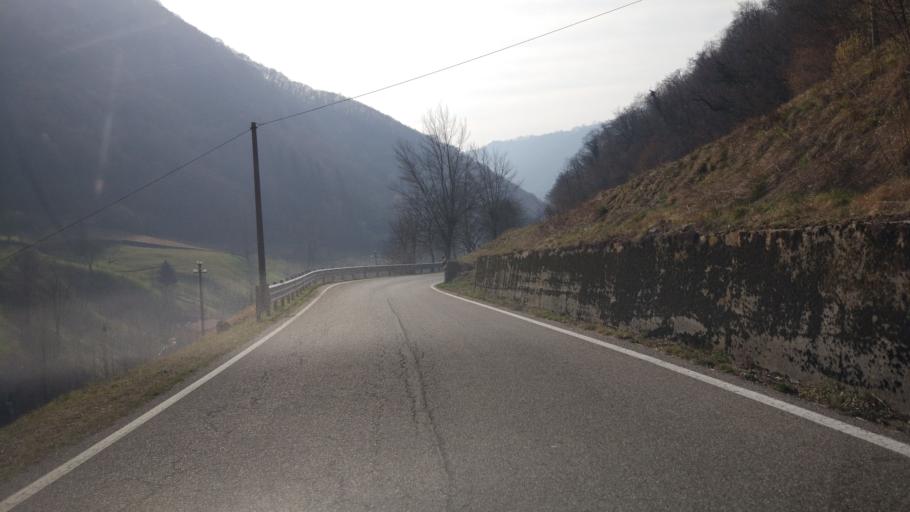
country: IT
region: Veneto
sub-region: Provincia di Verona
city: Selva di Progno
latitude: 45.6011
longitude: 11.1604
